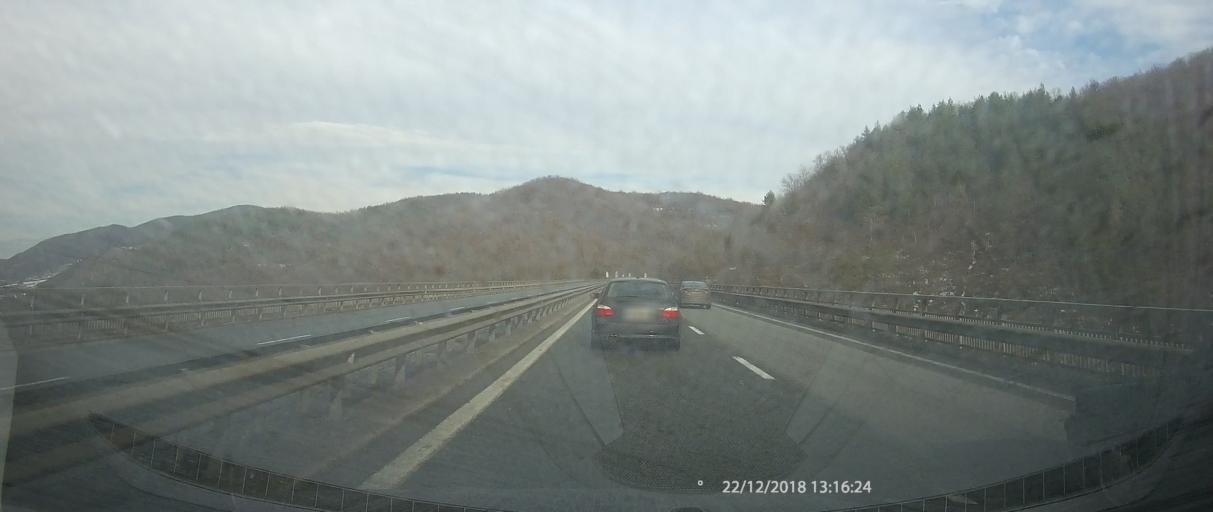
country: BG
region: Sofiya
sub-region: Obshtina Pravets
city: Pravets
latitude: 42.9233
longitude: 23.9220
